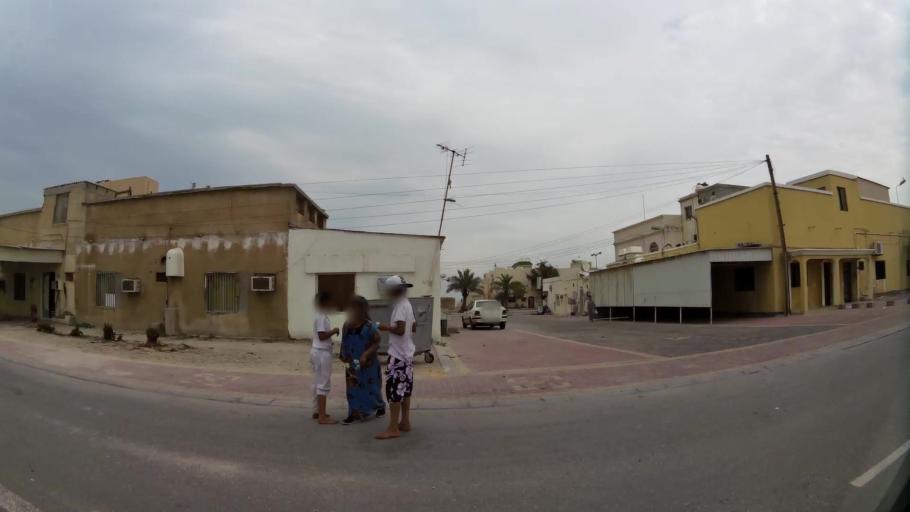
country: BH
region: Northern
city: Ar Rifa'
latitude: 26.0590
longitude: 50.6167
